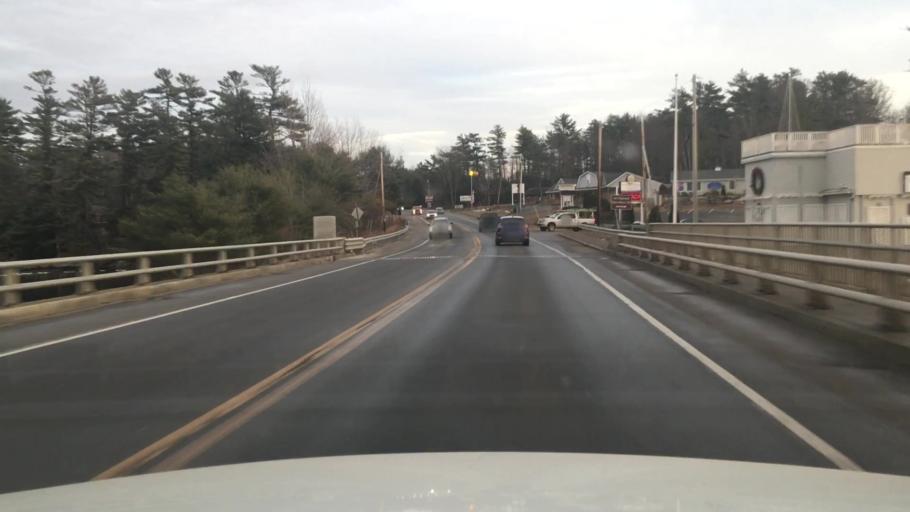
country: US
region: Maine
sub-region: Lincoln County
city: Wiscasset
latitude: 43.9999
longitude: -69.6528
